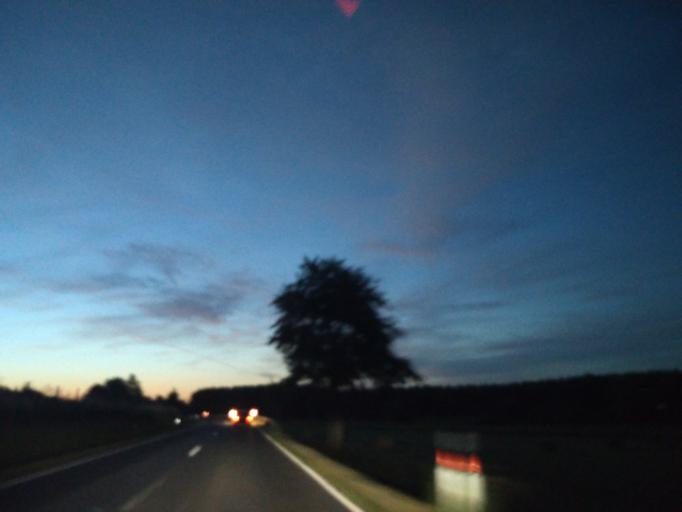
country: HU
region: Vas
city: Vasvar
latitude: 46.9747
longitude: 16.8429
